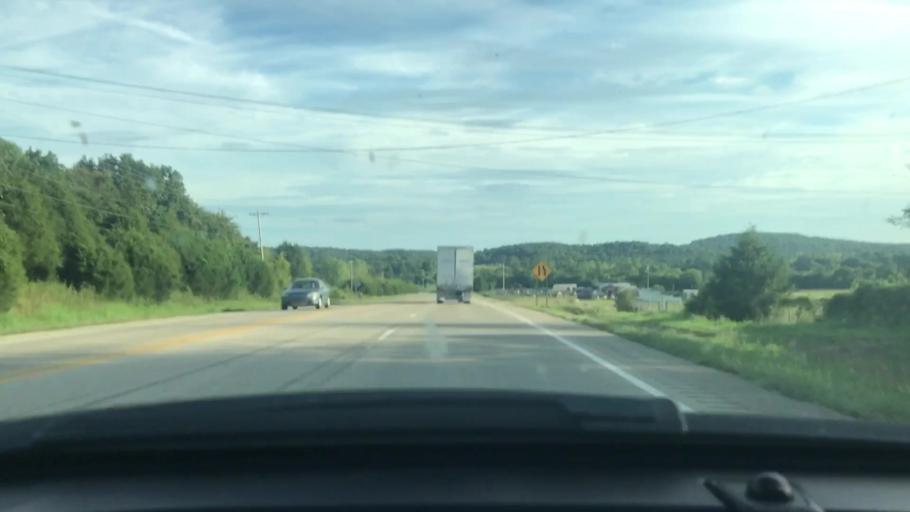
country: US
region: Arkansas
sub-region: Randolph County
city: Pocahontas
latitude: 36.1864
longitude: -91.1627
